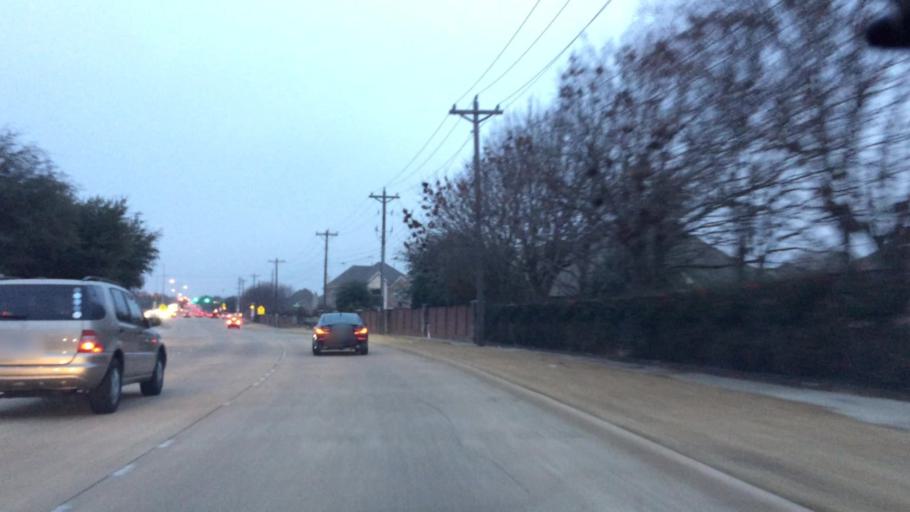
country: US
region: Texas
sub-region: Collin County
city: Frisco
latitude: 33.1035
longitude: -96.7716
